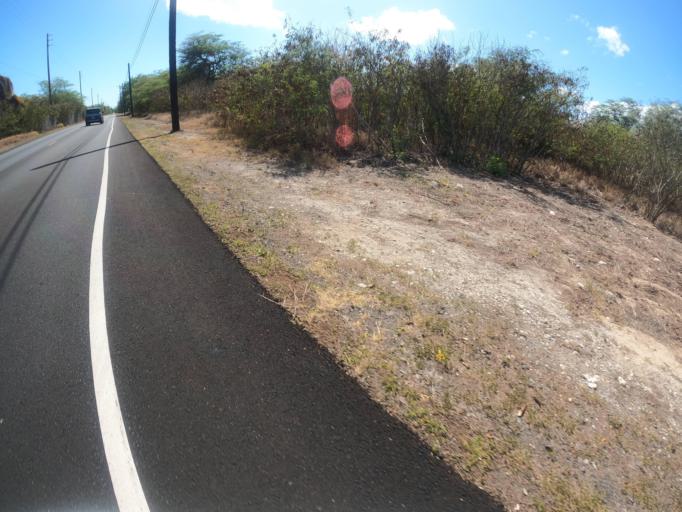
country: US
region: Hawaii
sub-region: Honolulu County
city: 'Ewa Villages
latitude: 21.3109
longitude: -158.0560
